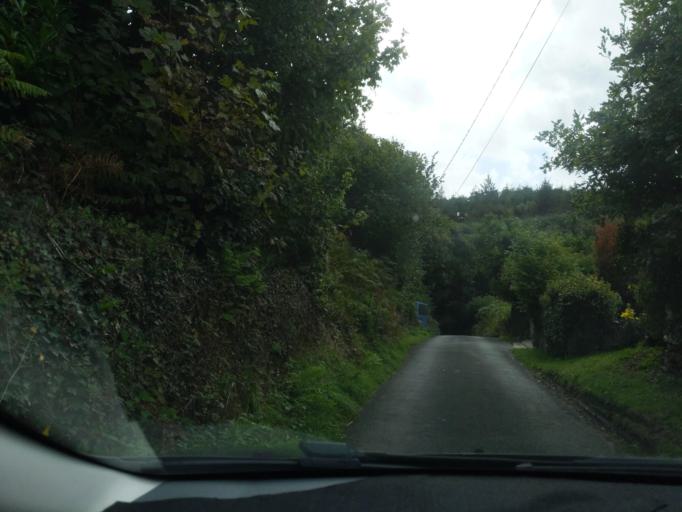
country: GB
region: England
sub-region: Cornwall
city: Lostwithiel
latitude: 50.3966
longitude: -4.7037
